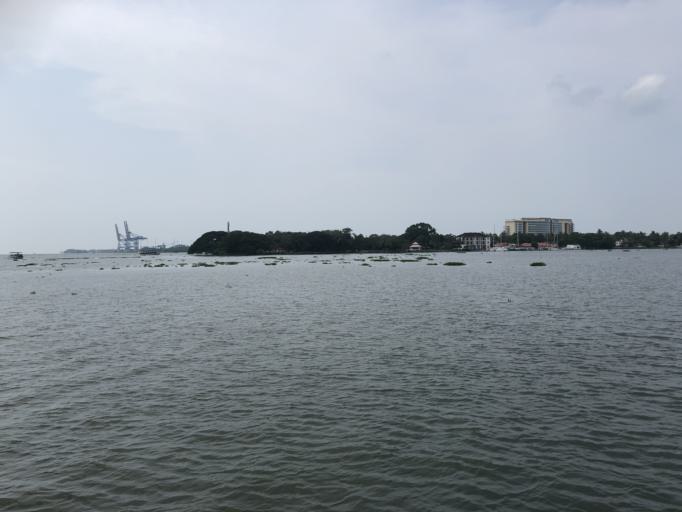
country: IN
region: Kerala
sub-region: Ernakulam
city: Cochin
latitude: 9.9835
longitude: 76.2725
